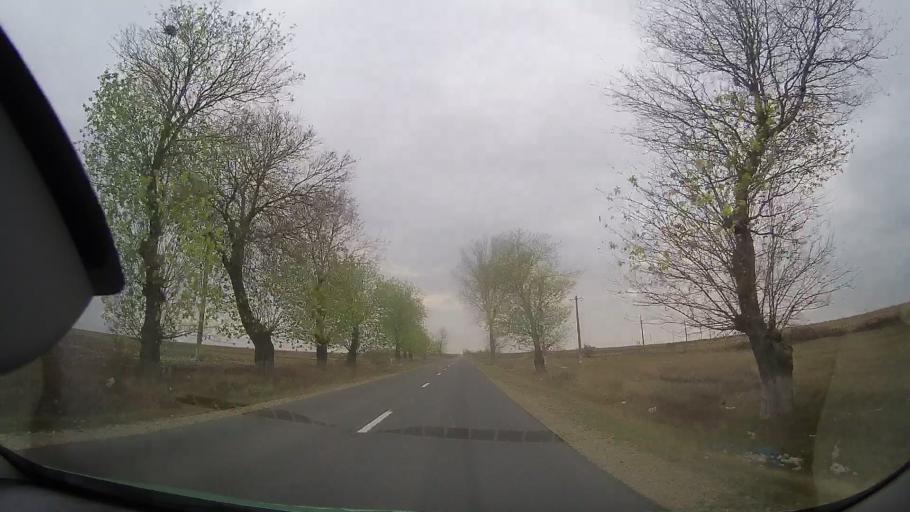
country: RO
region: Ialomita
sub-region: Comuna Garbovi
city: Garbovi
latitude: 44.7747
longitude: 26.7482
